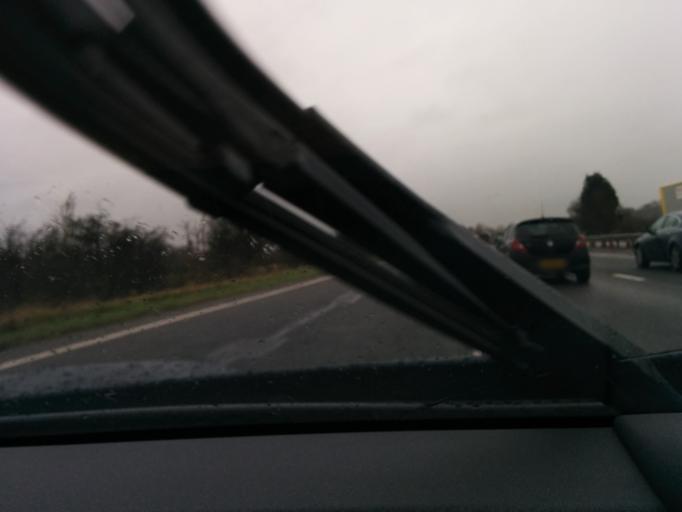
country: GB
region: England
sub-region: Oxfordshire
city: Abingdon
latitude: 51.6729
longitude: -1.3088
